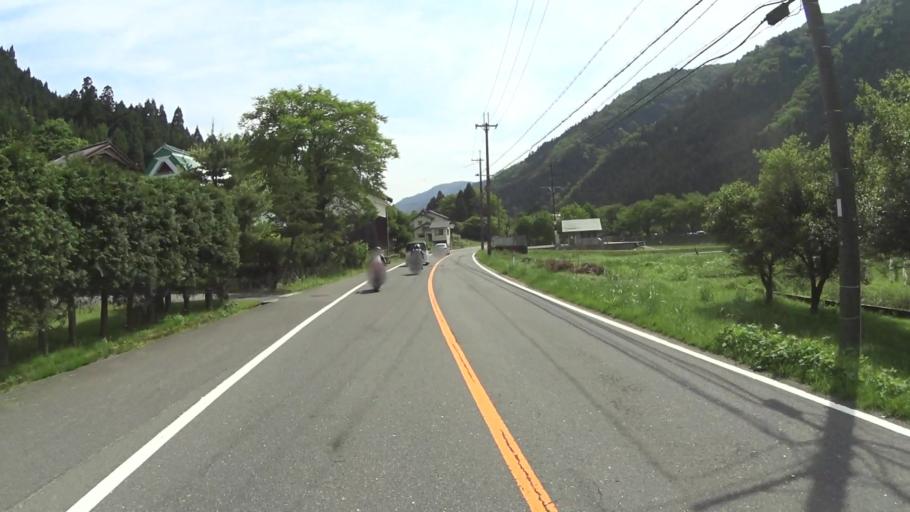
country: JP
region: Shiga Prefecture
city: Kitahama
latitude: 35.3257
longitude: 135.8993
